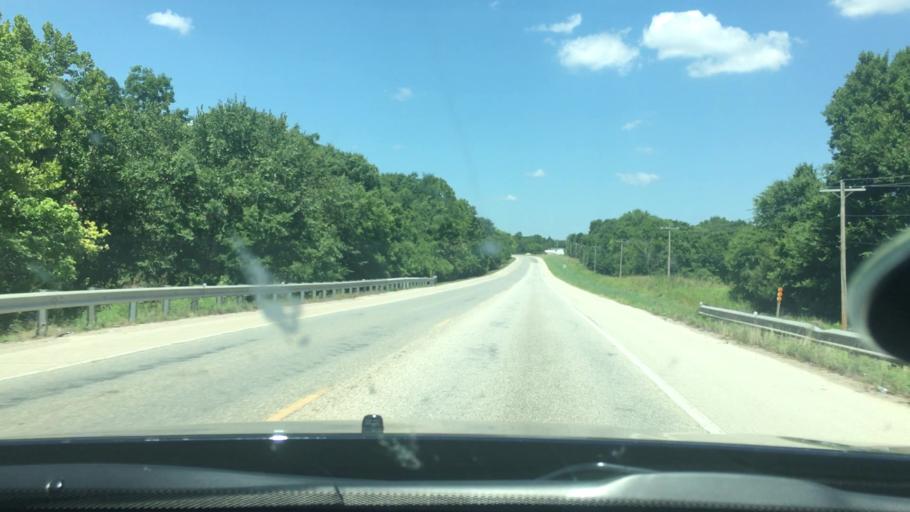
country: US
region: Oklahoma
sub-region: Marshall County
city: Oakland
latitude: 34.1820
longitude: -96.8678
